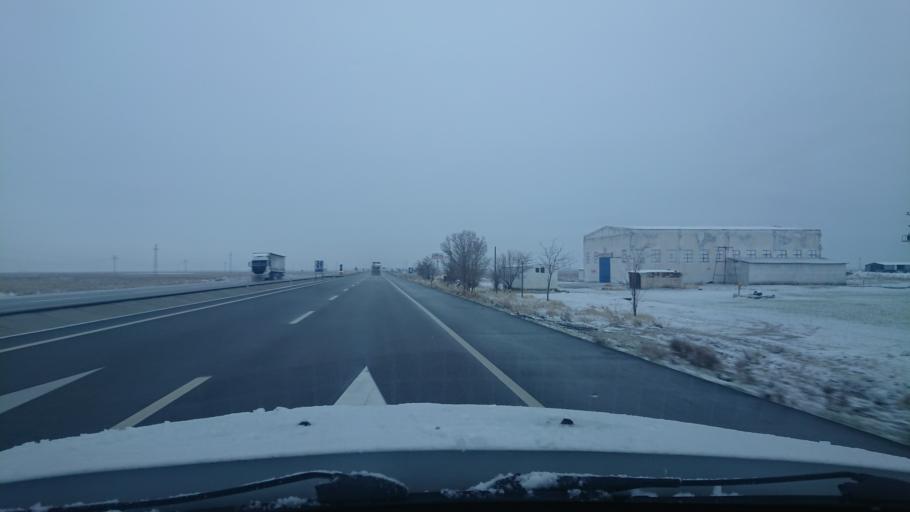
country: TR
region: Aksaray
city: Sultanhani
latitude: 38.2538
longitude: 33.5826
